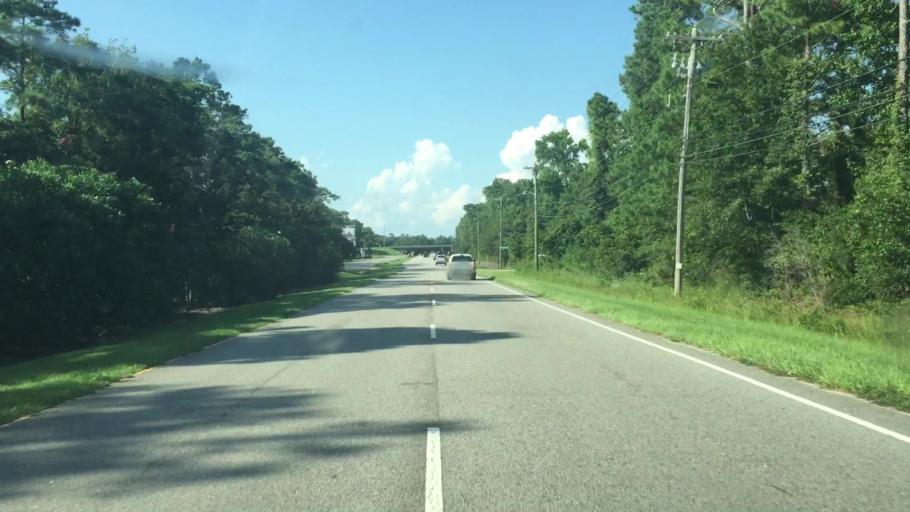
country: US
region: South Carolina
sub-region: Horry County
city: Myrtle Beach
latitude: 33.7616
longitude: -78.8063
